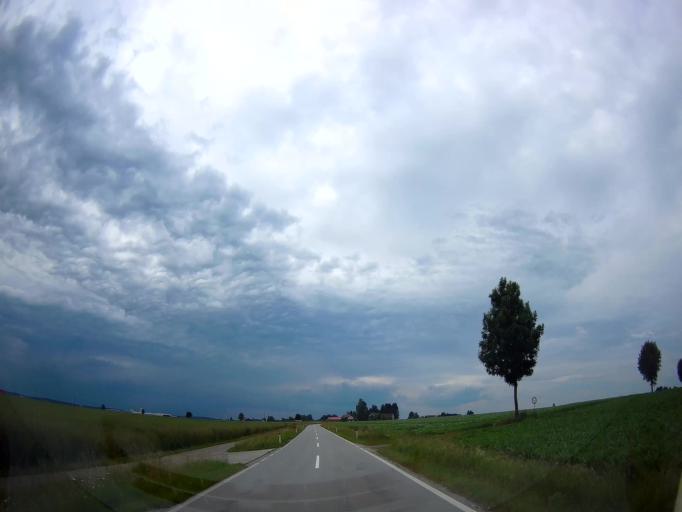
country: AT
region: Upper Austria
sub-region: Politischer Bezirk Braunau am Inn
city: Altheim
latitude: 48.2621
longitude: 13.2597
